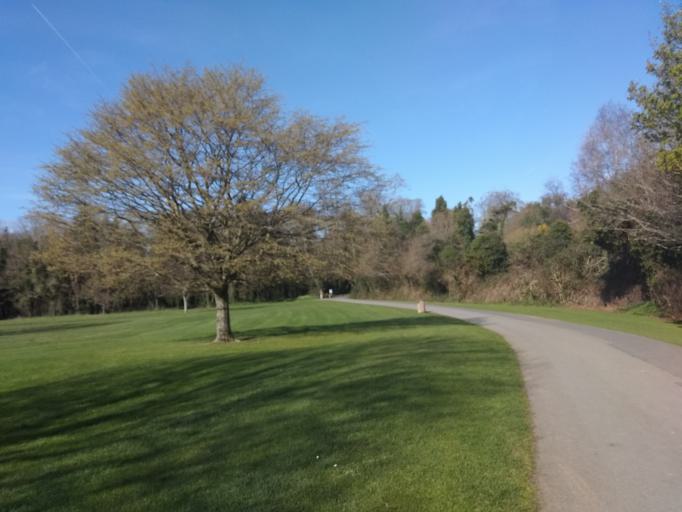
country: IE
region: Leinster
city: Malahide
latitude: 53.4442
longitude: -6.1664
